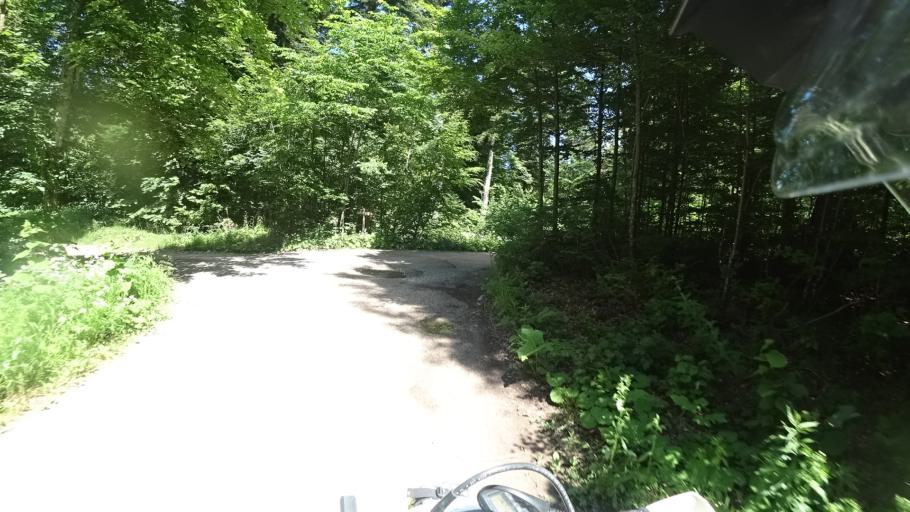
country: HR
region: Primorsko-Goranska
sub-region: Grad Delnice
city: Delnice
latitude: 45.4371
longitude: 14.7476
